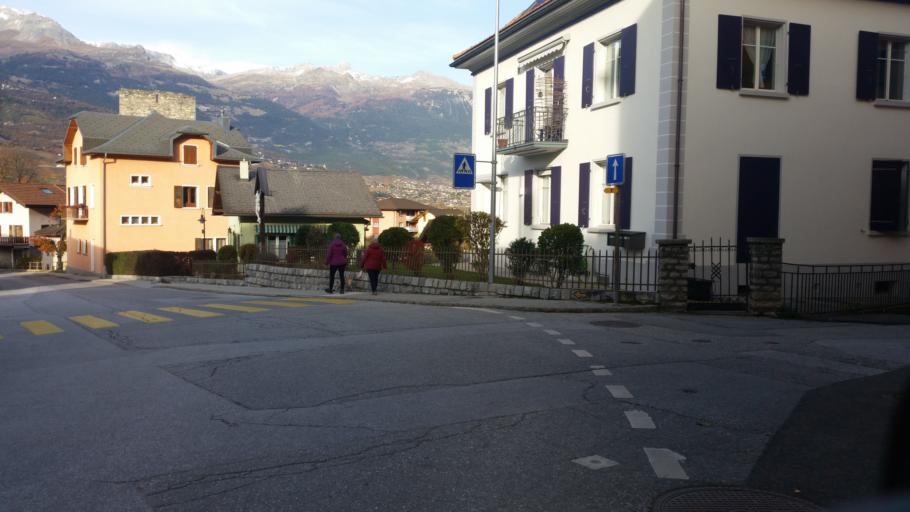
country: CH
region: Valais
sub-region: Sierre District
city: Chalais
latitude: 46.2659
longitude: 7.5089
